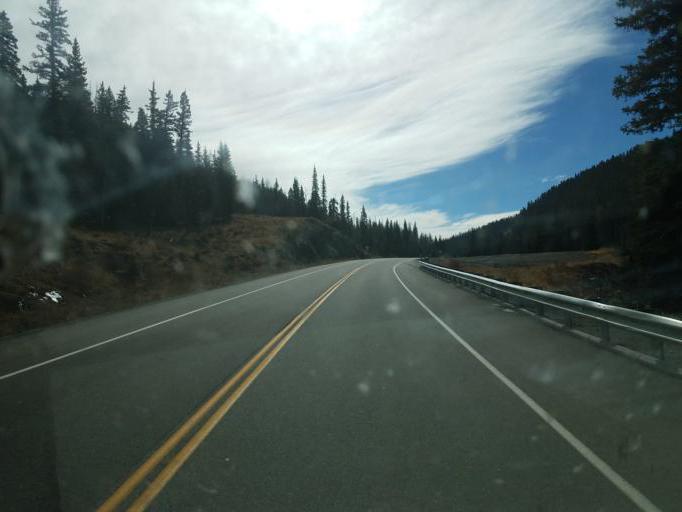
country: US
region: Colorado
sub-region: Mineral County
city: Creede
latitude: 37.5438
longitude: -106.7723
